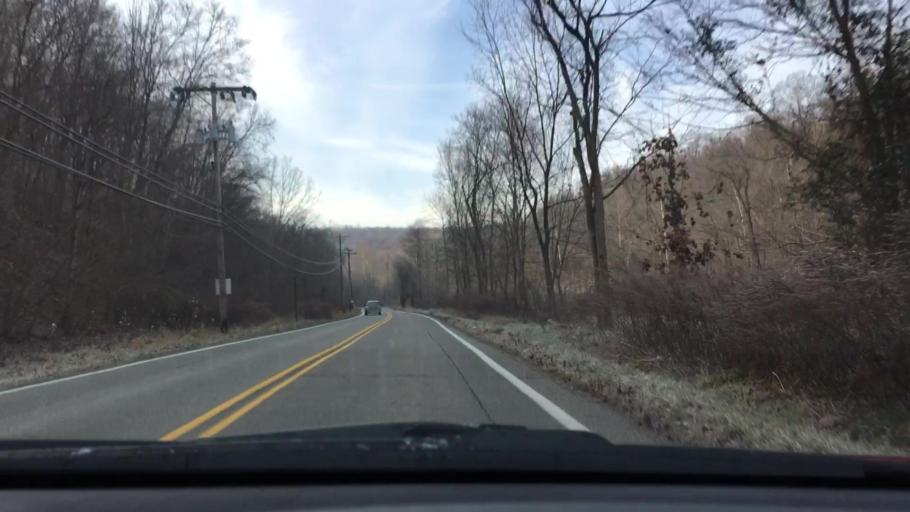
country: US
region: Pennsylvania
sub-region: Allegheny County
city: Industry
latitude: 40.2421
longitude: -79.8137
